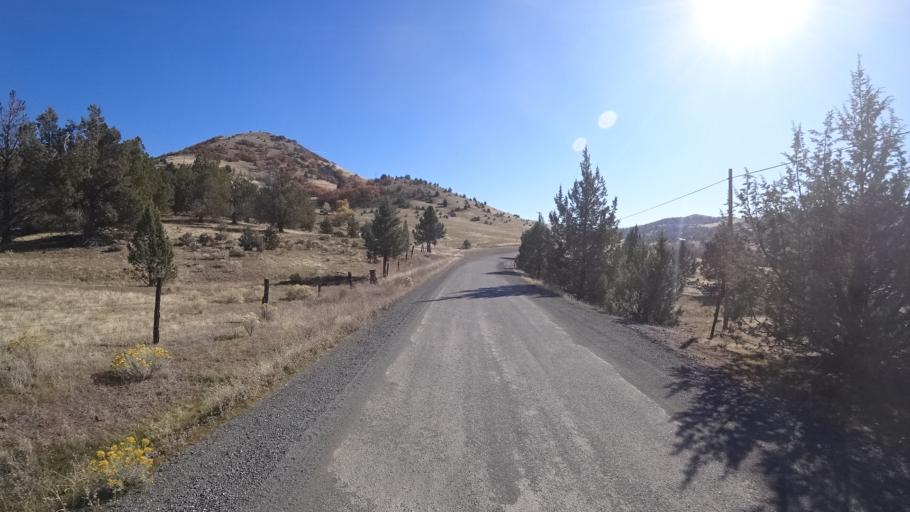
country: US
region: California
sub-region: Siskiyou County
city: Montague
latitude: 41.8014
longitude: -122.3691
